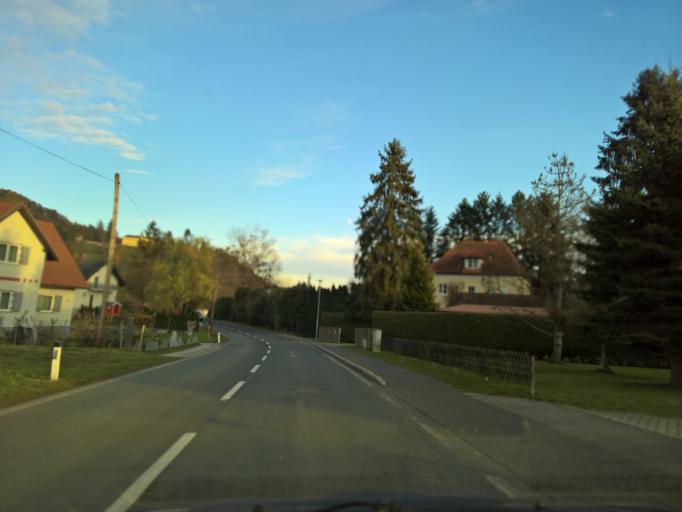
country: AT
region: Styria
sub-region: Politischer Bezirk Leibnitz
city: Arnfels
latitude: 46.6775
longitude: 15.3958
